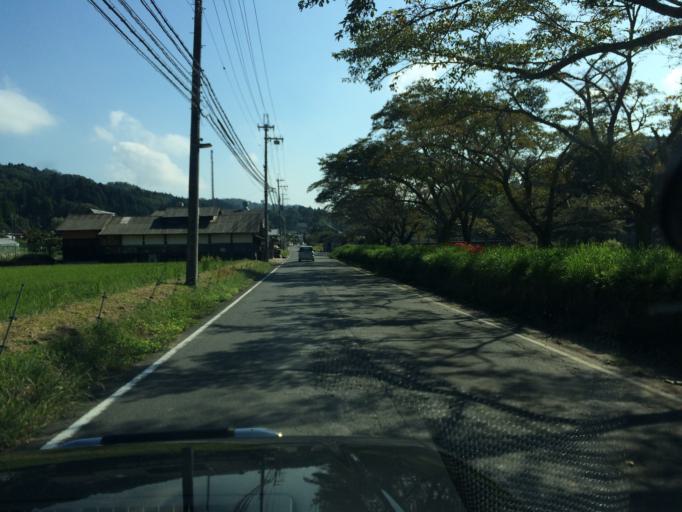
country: JP
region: Mie
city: Ueno-ebisumachi
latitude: 34.7352
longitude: 135.9659
